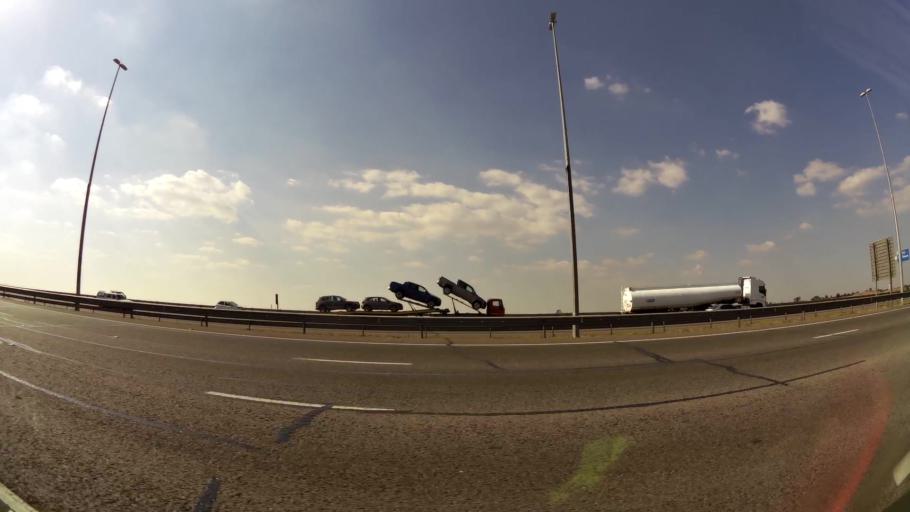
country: ZA
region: Gauteng
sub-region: Ekurhuleni Metropolitan Municipality
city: Tembisa
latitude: -26.0565
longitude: 28.2807
